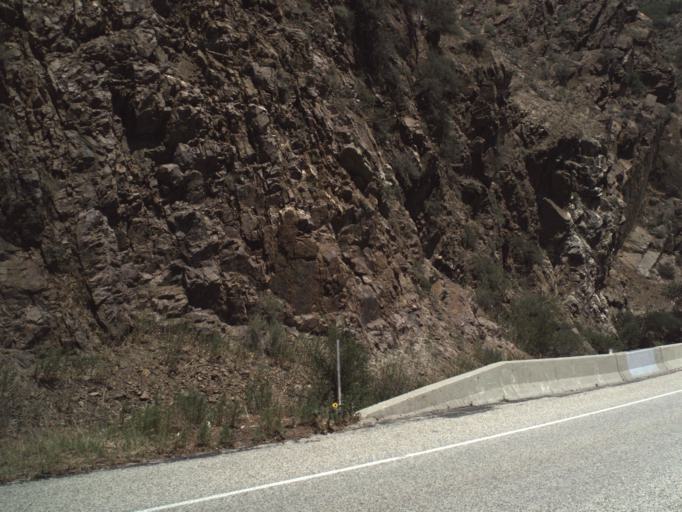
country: US
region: Utah
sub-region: Weber County
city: Ogden
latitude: 41.2360
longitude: -111.9270
